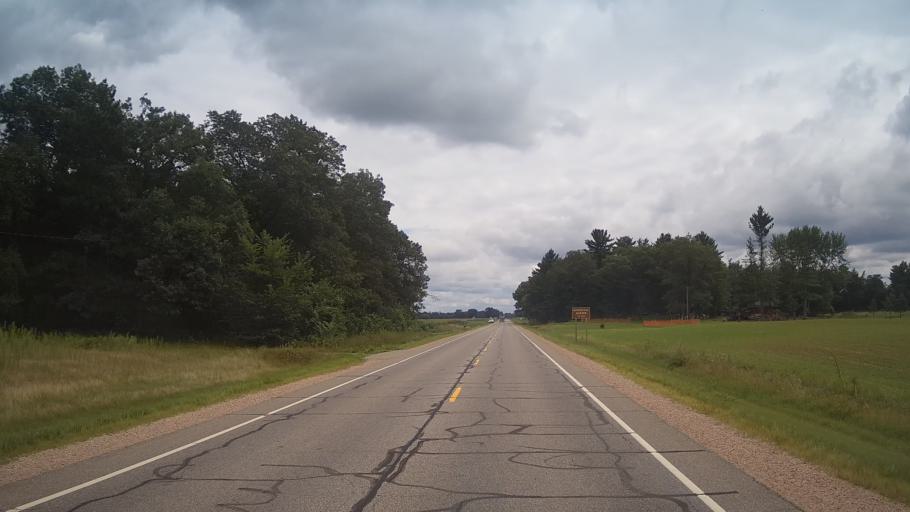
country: US
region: Wisconsin
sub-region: Adams County
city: Friendship
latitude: 44.0394
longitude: -89.9271
